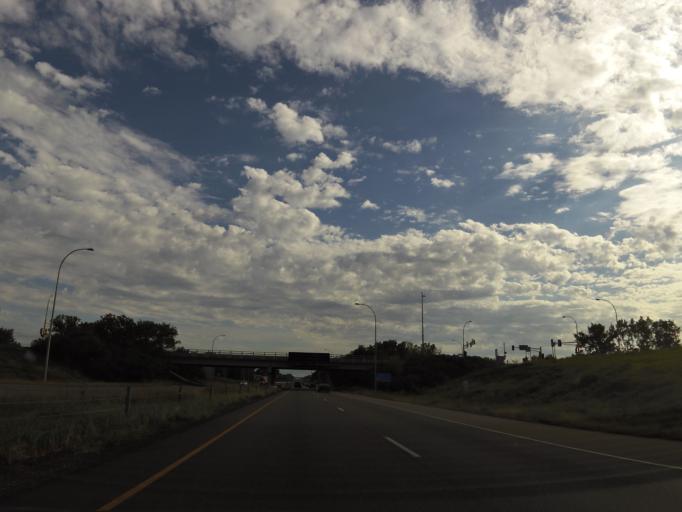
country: US
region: Minnesota
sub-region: Hennepin County
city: New Hope
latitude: 45.0451
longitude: -93.4010
